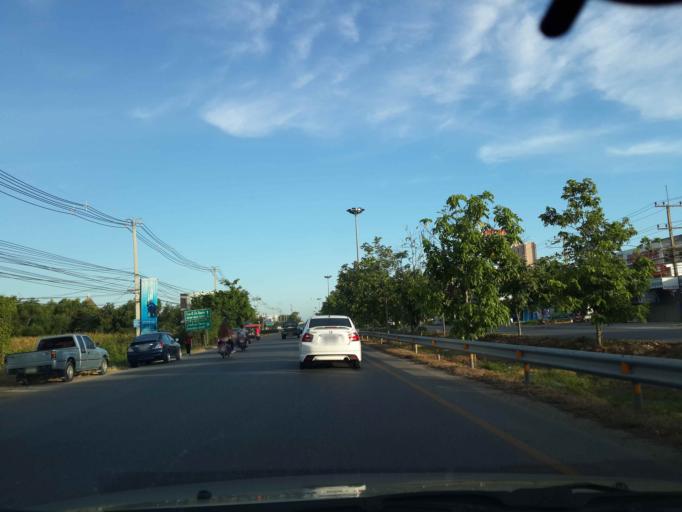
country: TH
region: Chon Buri
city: Phatthaya
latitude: 12.8493
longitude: 100.9092
